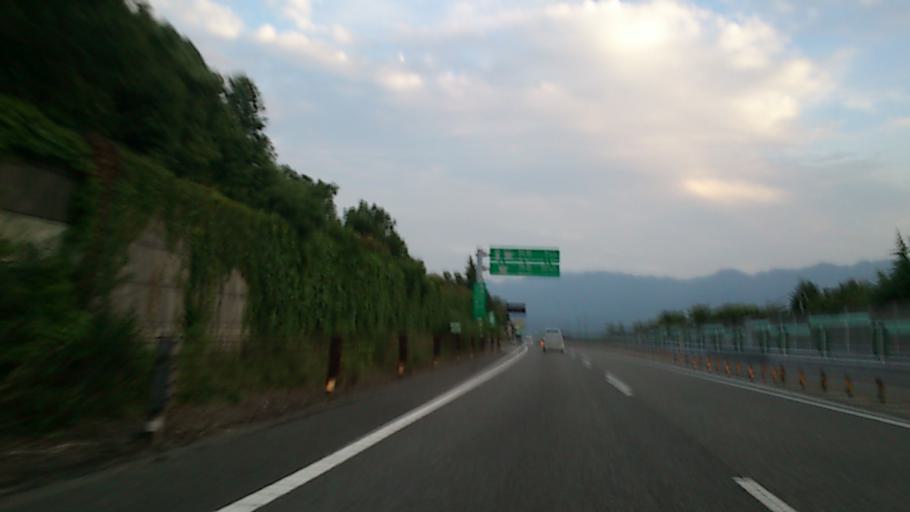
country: JP
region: Nagano
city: Iida
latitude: 35.4749
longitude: 137.7599
